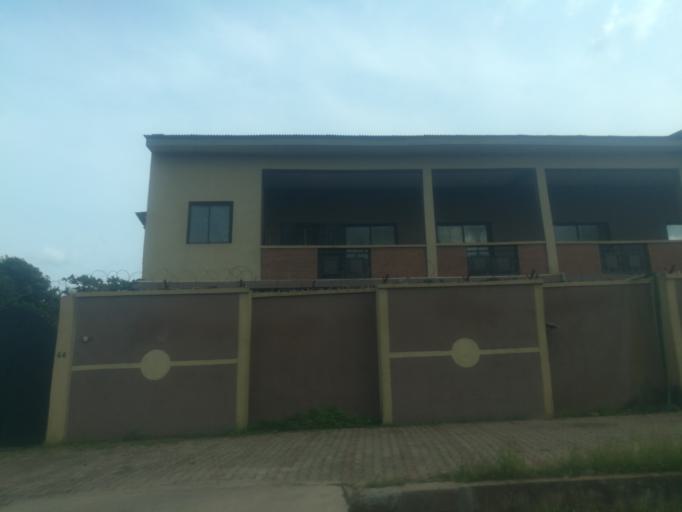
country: NG
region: Ogun
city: Abeokuta
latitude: 7.1307
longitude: 3.3214
